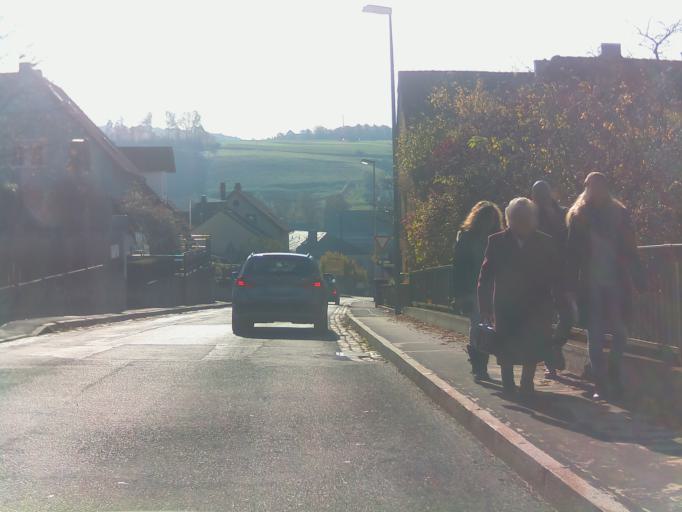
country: DE
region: Bavaria
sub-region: Regierungsbezirk Unterfranken
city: Geiselwind
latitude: 49.8493
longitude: 10.4976
